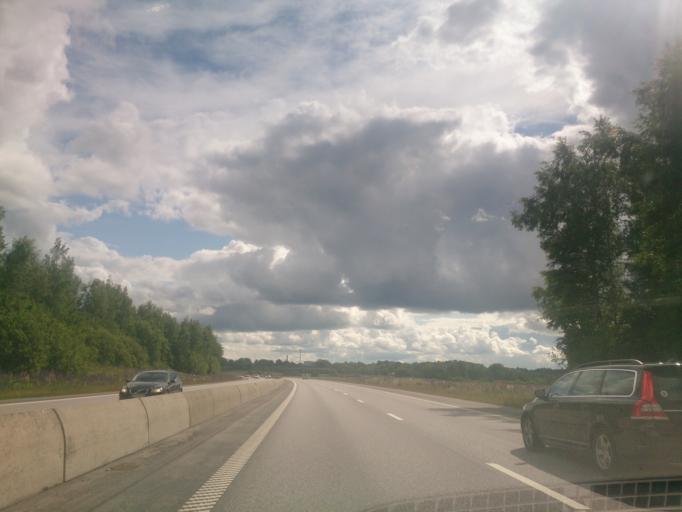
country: SE
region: OEstergoetland
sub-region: Norrkopings Kommun
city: Norrkoping
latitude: 58.6062
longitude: 16.1294
